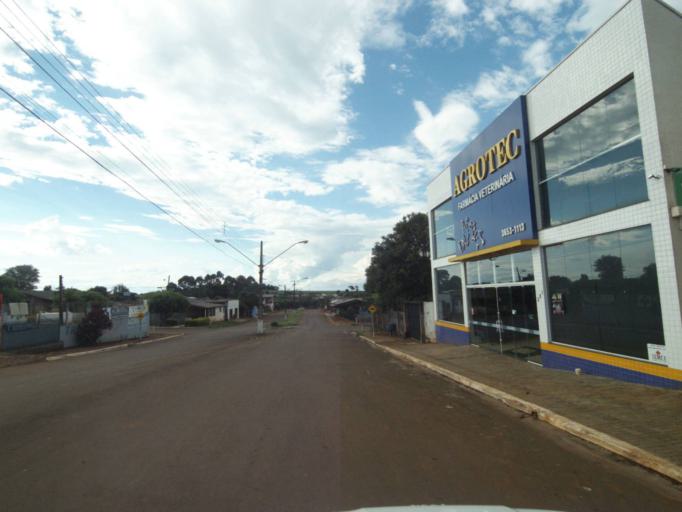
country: BR
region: Parana
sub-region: Laranjeiras Do Sul
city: Laranjeiras do Sul
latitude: -25.4918
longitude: -52.5296
